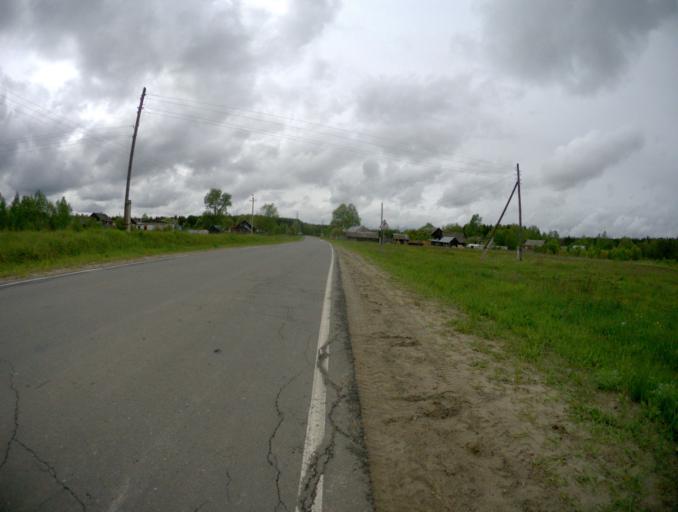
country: RU
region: Vladimir
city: Velikodvorskiy
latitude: 55.3876
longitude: 40.7435
